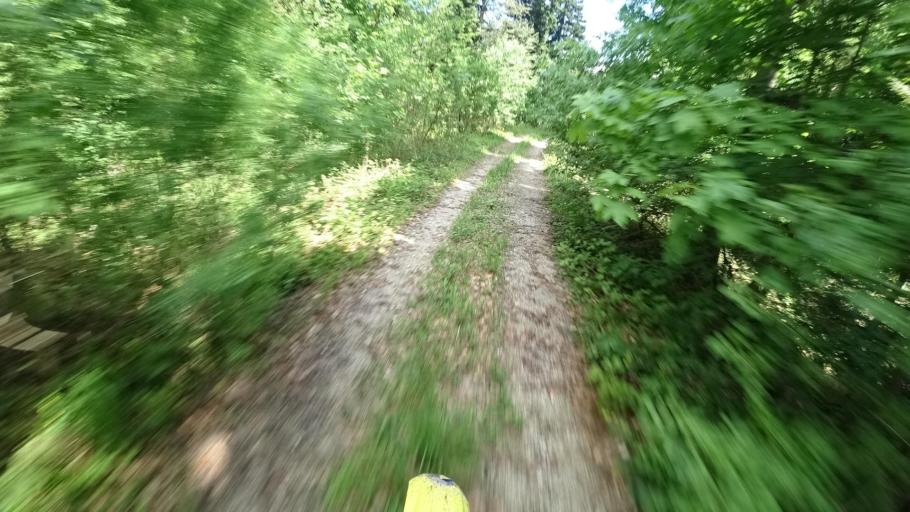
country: BA
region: Federation of Bosnia and Herzegovina
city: Bosanska Krupa
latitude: 44.7622
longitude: 16.1343
